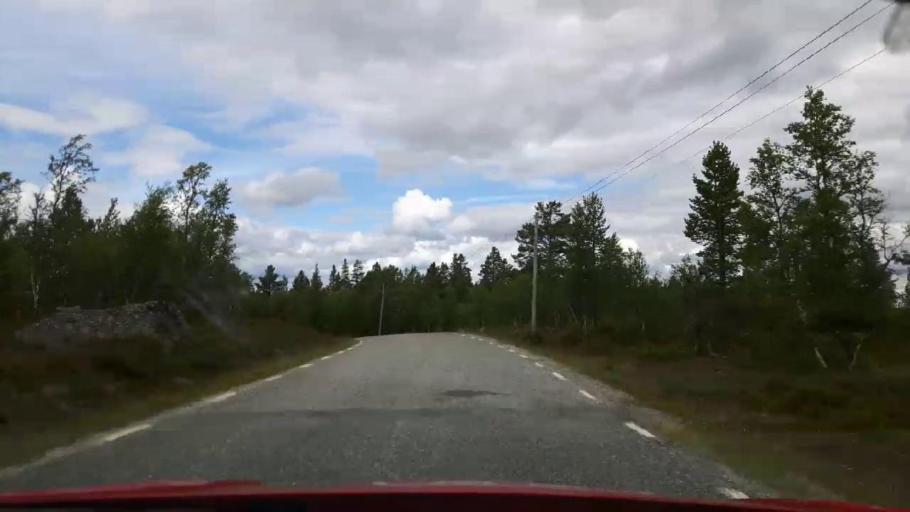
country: NO
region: Hedmark
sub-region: Engerdal
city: Engerdal
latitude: 62.3508
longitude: 12.7949
